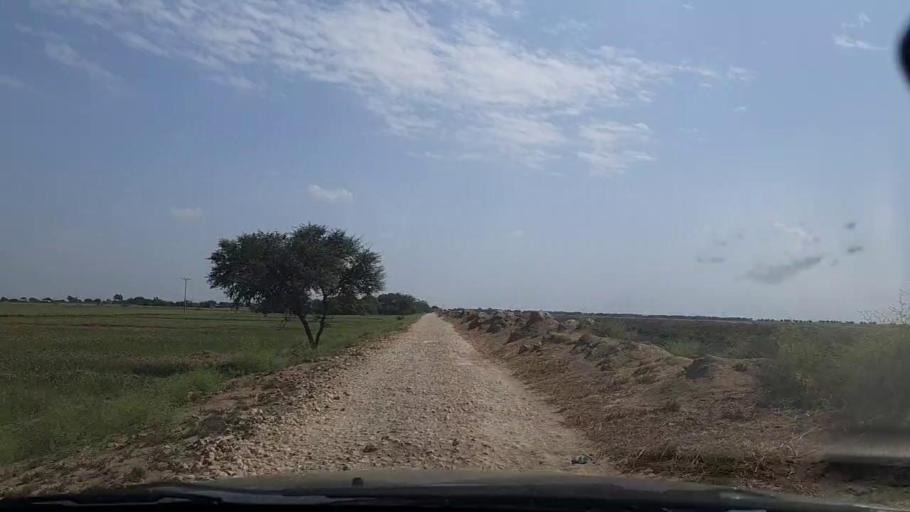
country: PK
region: Sindh
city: Mirpur Batoro
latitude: 24.5764
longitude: 68.1963
